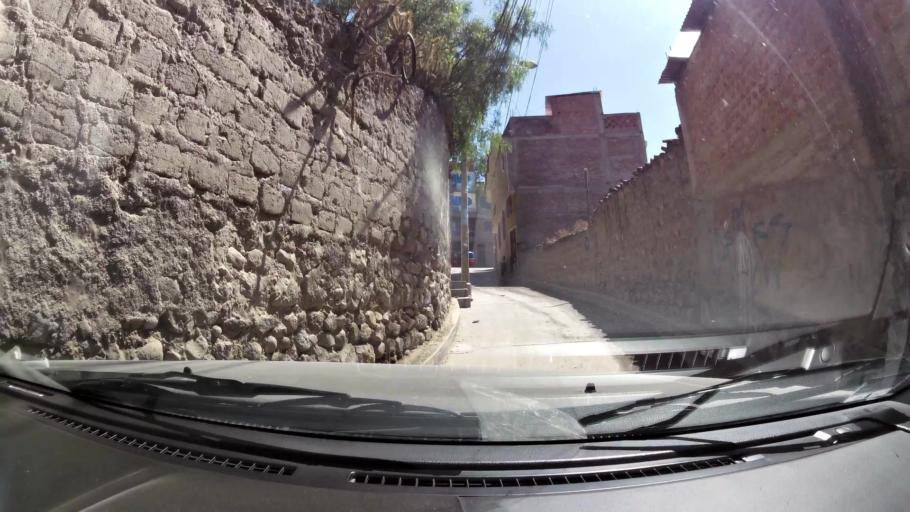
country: PE
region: Ayacucho
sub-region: Provincia de Huamanga
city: Ayacucho
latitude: -13.1665
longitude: -74.2312
